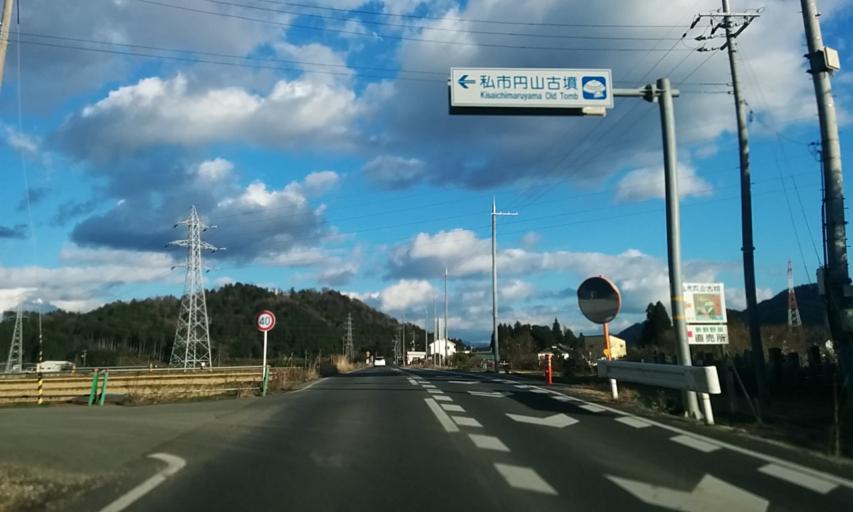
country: JP
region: Kyoto
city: Ayabe
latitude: 35.3124
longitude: 135.1962
